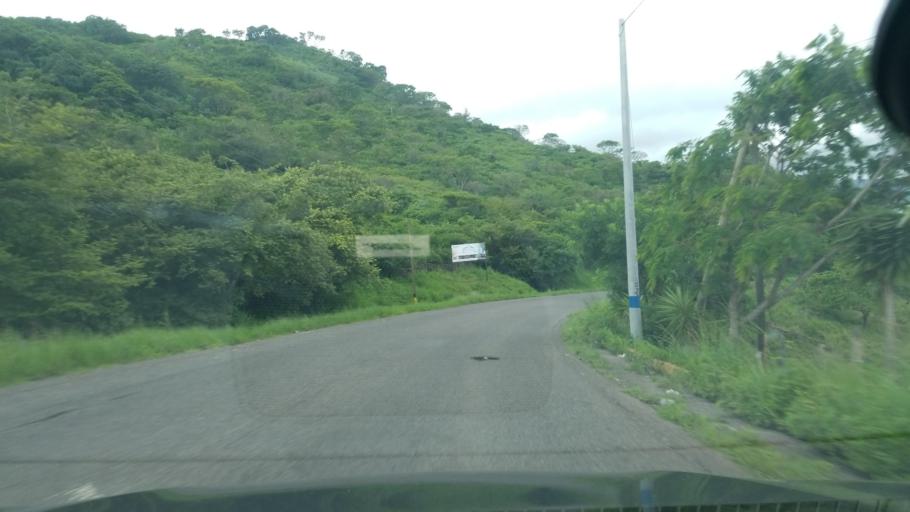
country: HN
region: Choluteca
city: San Marcos de Colon
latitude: 13.4311
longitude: -86.8272
